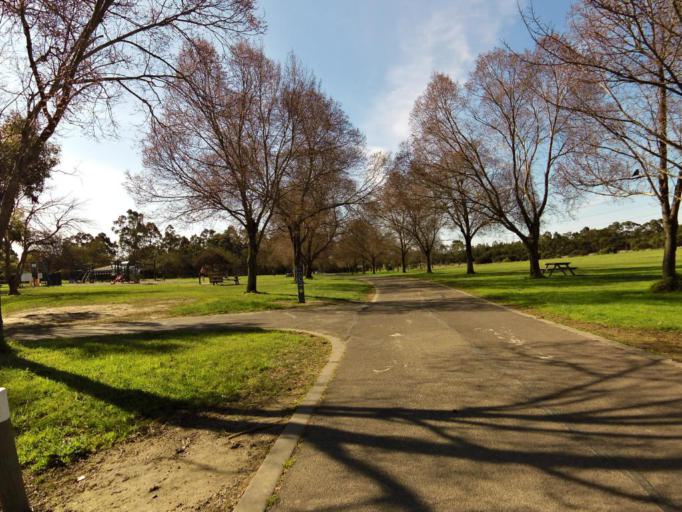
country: AU
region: Victoria
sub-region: Monash
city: Mulgrave
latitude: -37.9054
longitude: 145.2012
